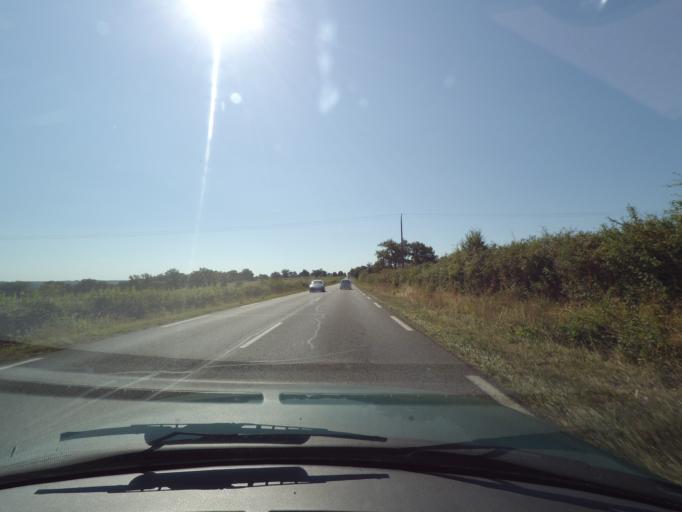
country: FR
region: Limousin
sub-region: Departement de la Haute-Vienne
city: Peyrat-de-Bellac
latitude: 46.1439
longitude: 0.9737
